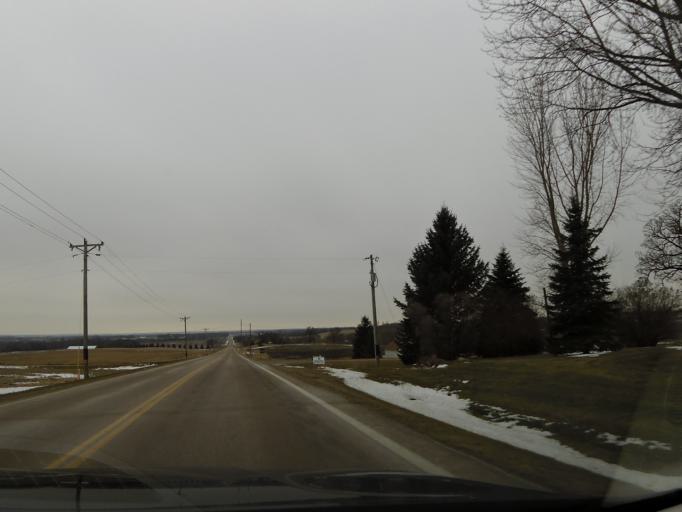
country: US
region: Minnesota
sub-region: Carver County
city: Carver
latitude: 44.7615
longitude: -93.6838
